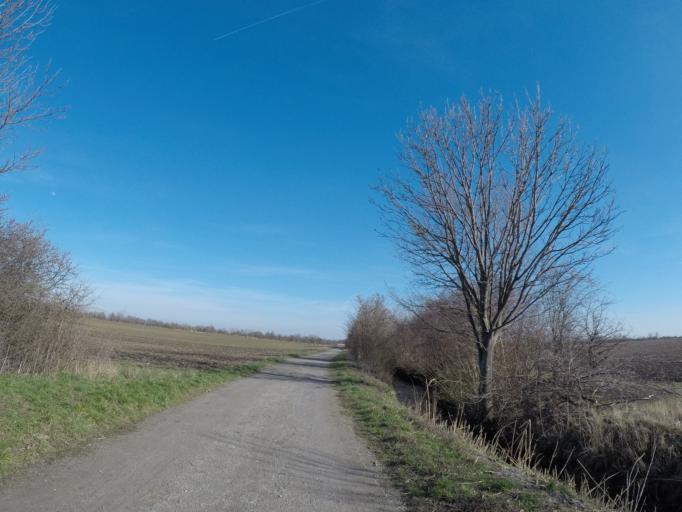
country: AT
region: Lower Austria
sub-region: Politischer Bezirk Modling
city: Biedermannsdorf
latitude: 48.1005
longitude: 16.3348
